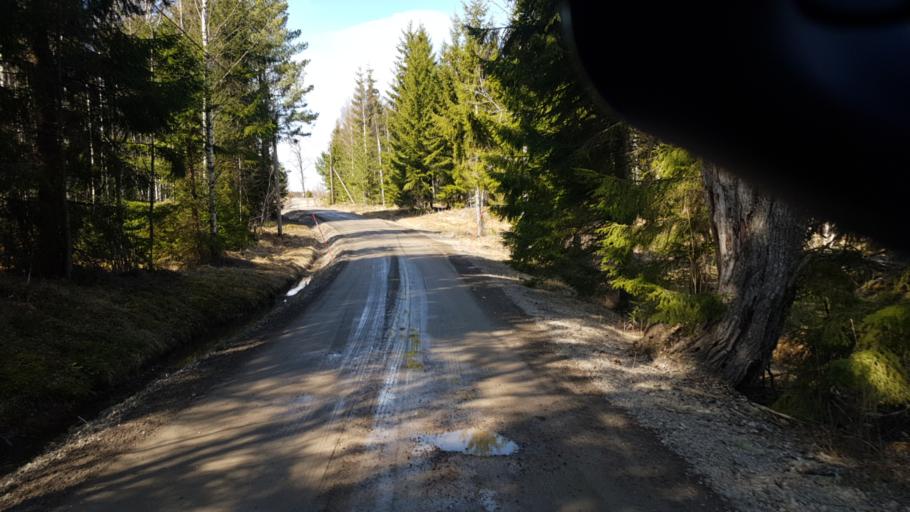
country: SE
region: Vaermland
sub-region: Arvika Kommun
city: Arvika
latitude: 59.5428
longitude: 12.8565
